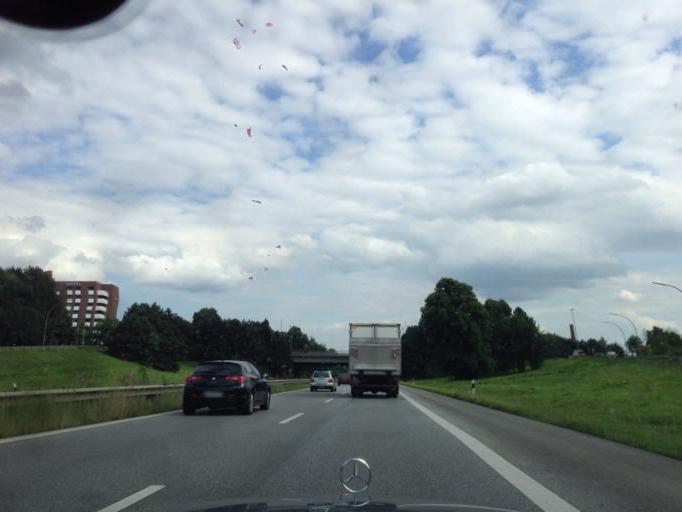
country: DE
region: Hamburg
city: Wandsbek
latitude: 53.5398
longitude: 10.0970
